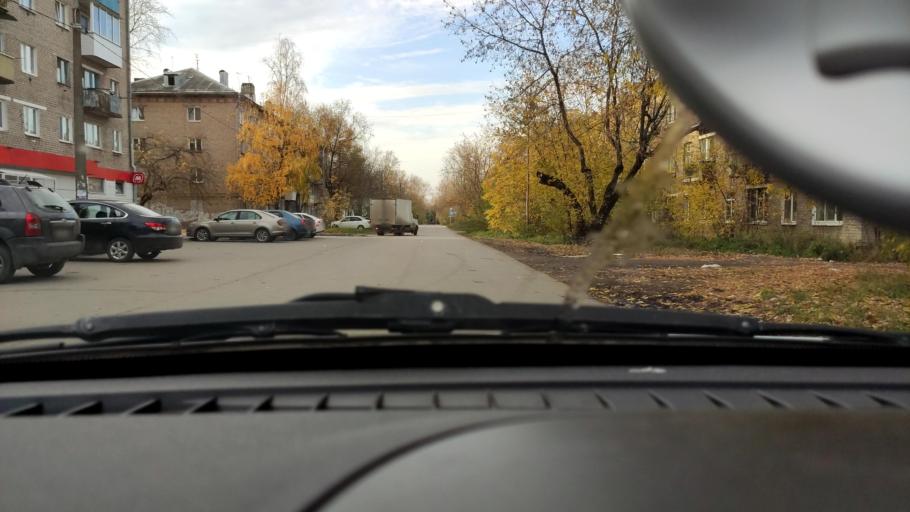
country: RU
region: Perm
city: Perm
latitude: 58.0882
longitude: 56.3917
